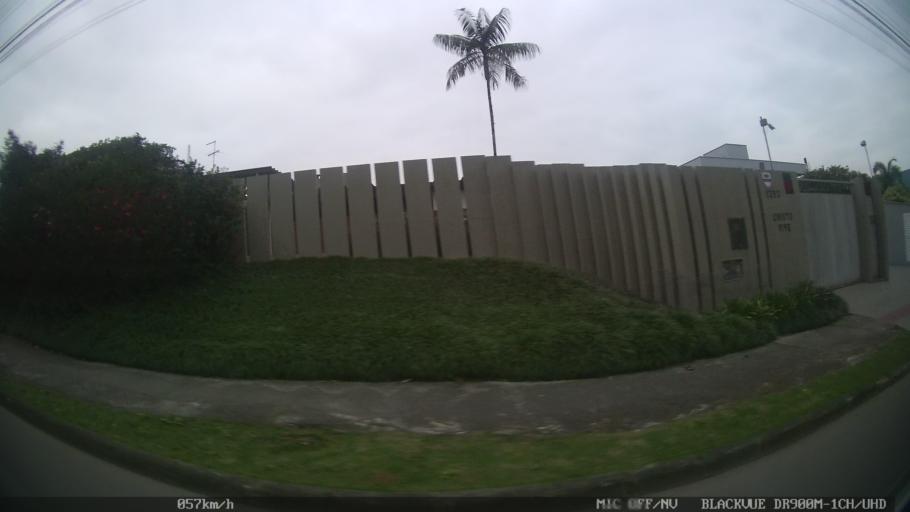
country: BR
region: Santa Catarina
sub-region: Joinville
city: Joinville
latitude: -26.2782
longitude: -48.8601
